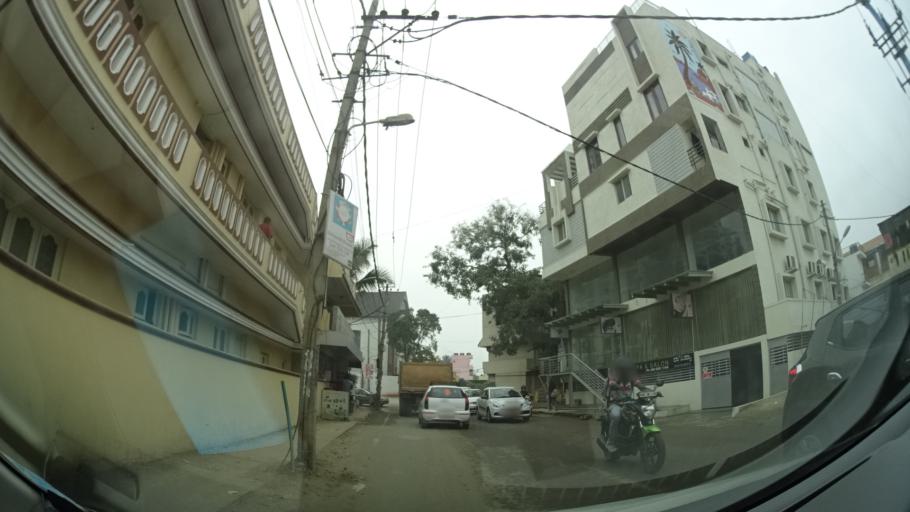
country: IN
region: Karnataka
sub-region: Bangalore Rural
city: Hoskote
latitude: 12.9699
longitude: 77.7349
